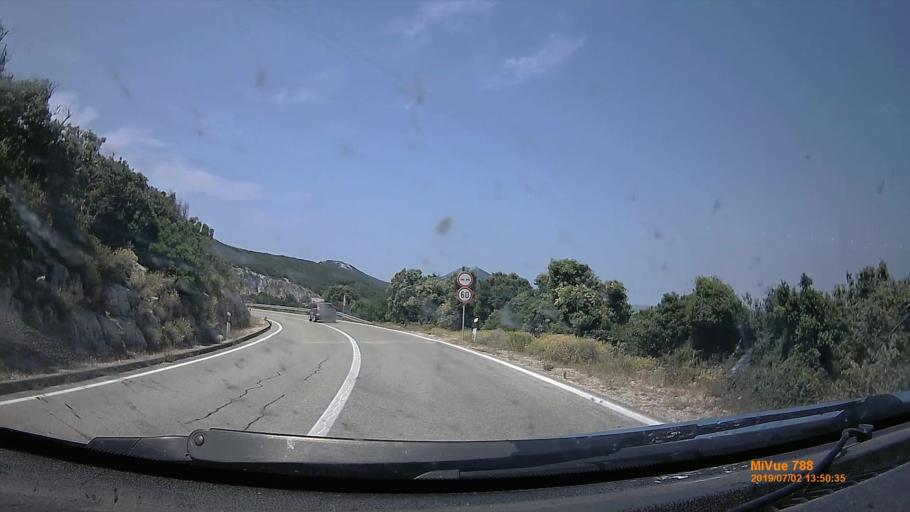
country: HR
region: Primorsko-Goranska
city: Mali Losinj
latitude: 44.5981
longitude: 14.4095
